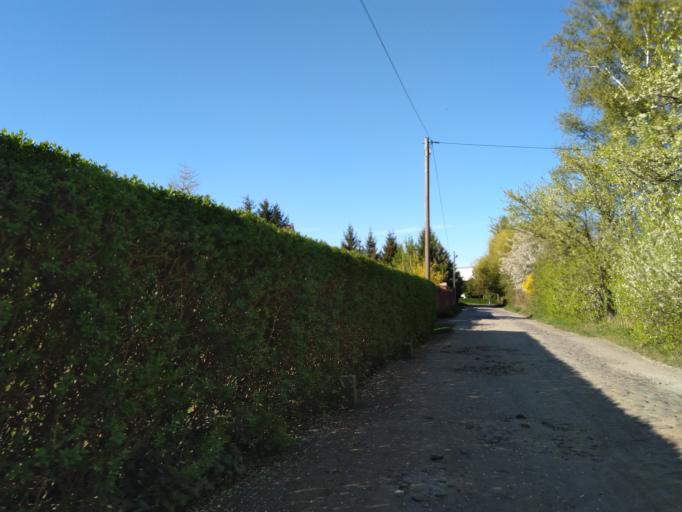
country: DE
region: Brandenburg
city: Wriezen
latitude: 52.7134
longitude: 14.1383
